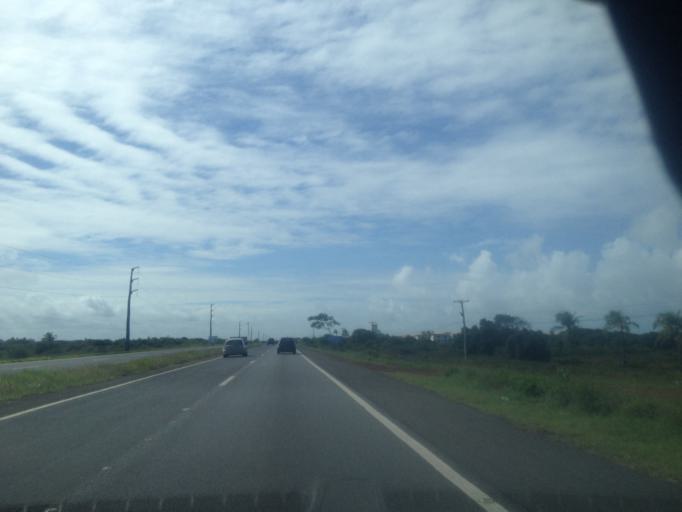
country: BR
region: Bahia
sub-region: Camacari
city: Camacari
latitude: -12.6677
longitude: -38.0958
